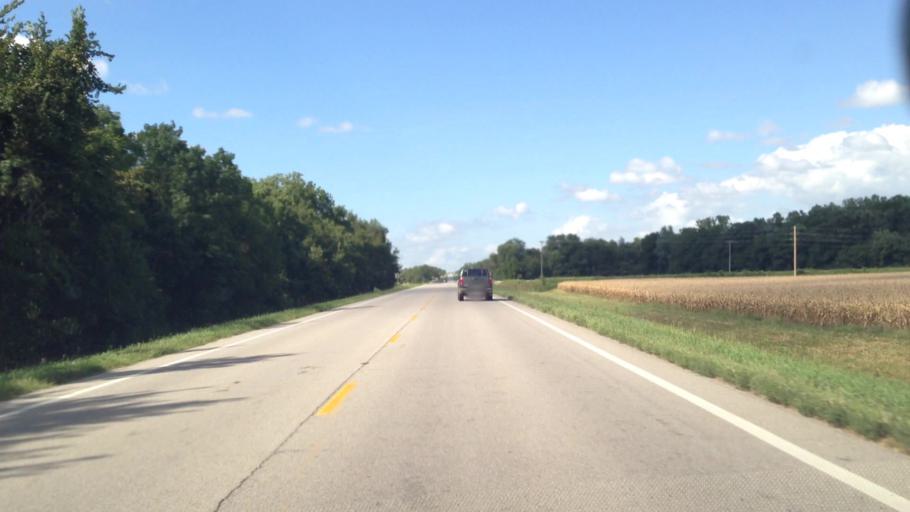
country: US
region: Kansas
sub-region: Neosho County
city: Erie
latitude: 37.6283
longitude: -95.2518
